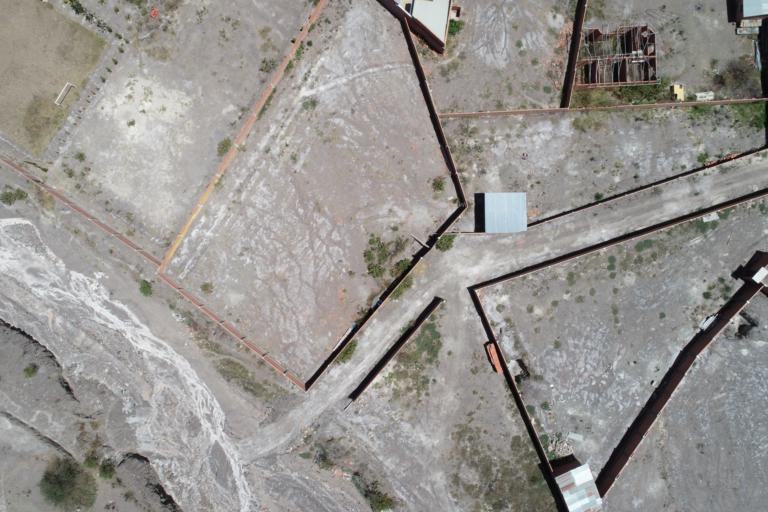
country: BO
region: La Paz
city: La Paz
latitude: -16.6416
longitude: -68.0412
